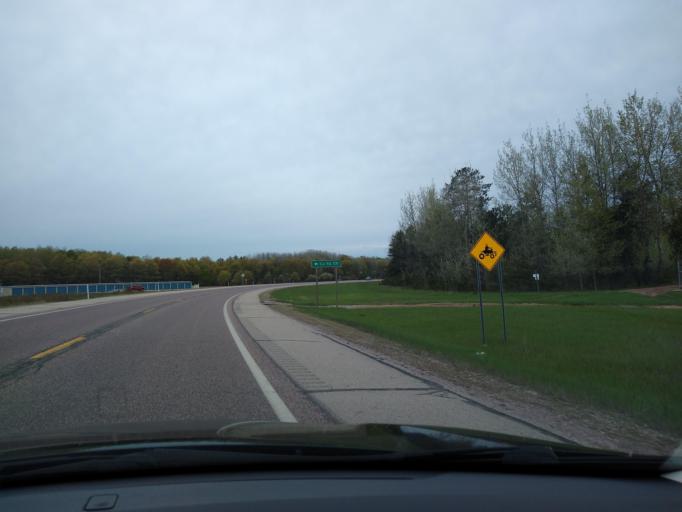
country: US
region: Michigan
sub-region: Delta County
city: Gladstone
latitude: 45.8560
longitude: -87.0595
